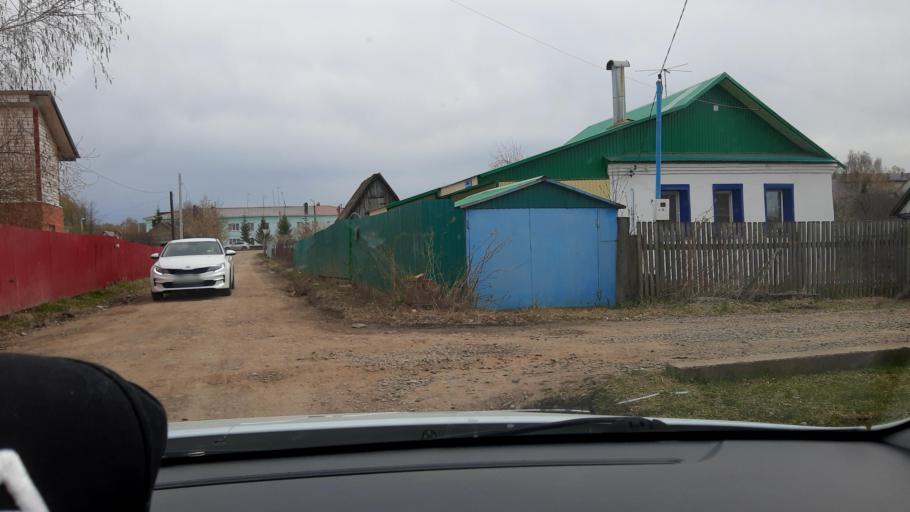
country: RU
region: Bashkortostan
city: Iglino
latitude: 54.8338
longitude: 56.4087
